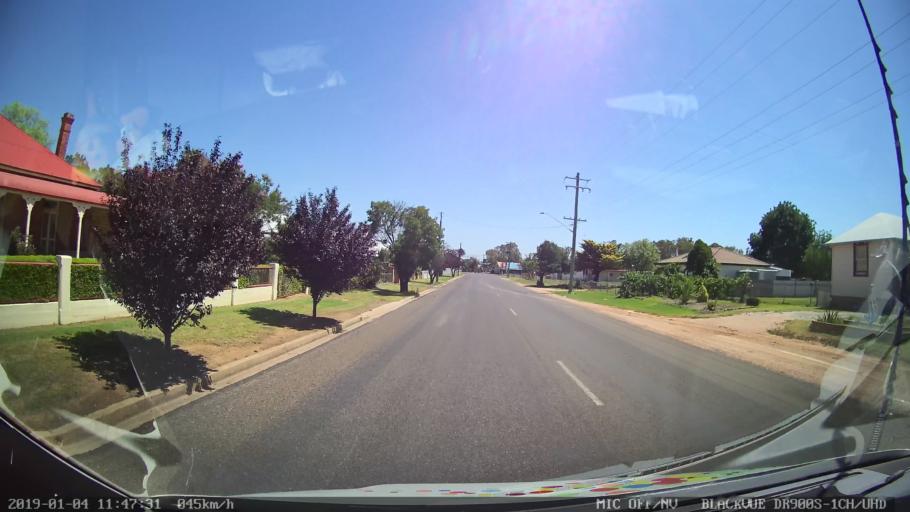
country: AU
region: New South Wales
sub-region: Cabonne
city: Molong
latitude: -32.9323
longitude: 148.7549
